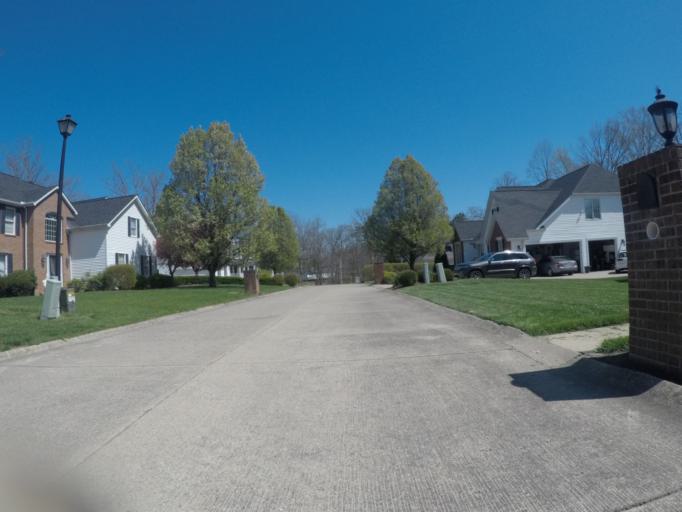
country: US
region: West Virginia
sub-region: Cabell County
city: Pea Ridge
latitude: 38.4221
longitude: -82.3176
